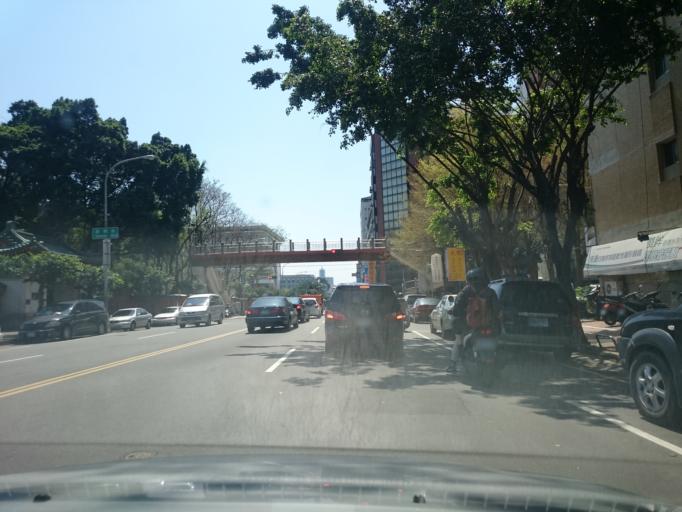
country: TW
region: Taiwan
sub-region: Taichung City
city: Taichung
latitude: 24.1542
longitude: 120.6894
